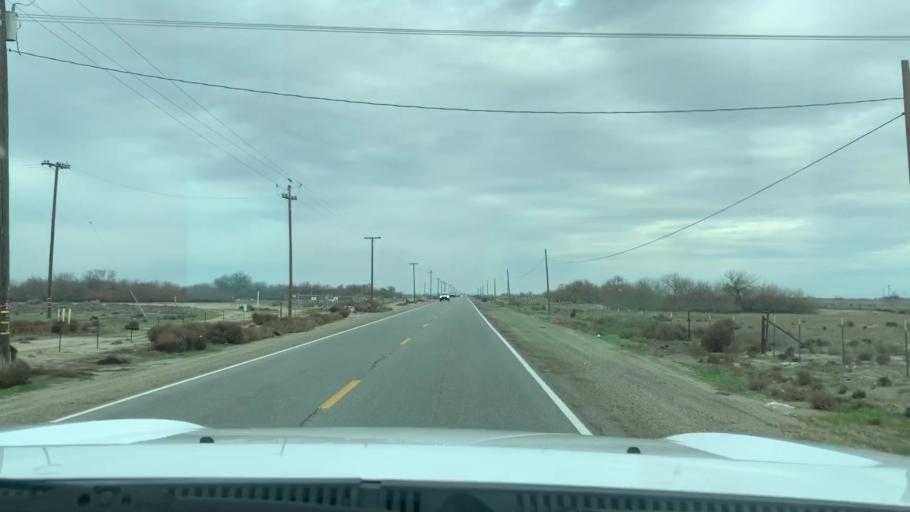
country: US
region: California
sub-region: Kern County
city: Rosedale
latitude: 35.3198
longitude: -119.2524
